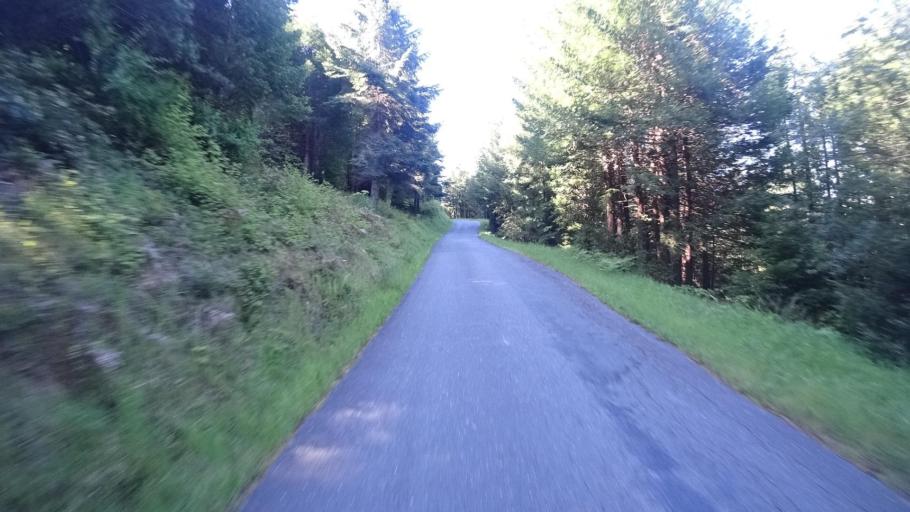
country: US
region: California
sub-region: Humboldt County
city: Rio Dell
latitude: 40.4539
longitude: -124.0266
